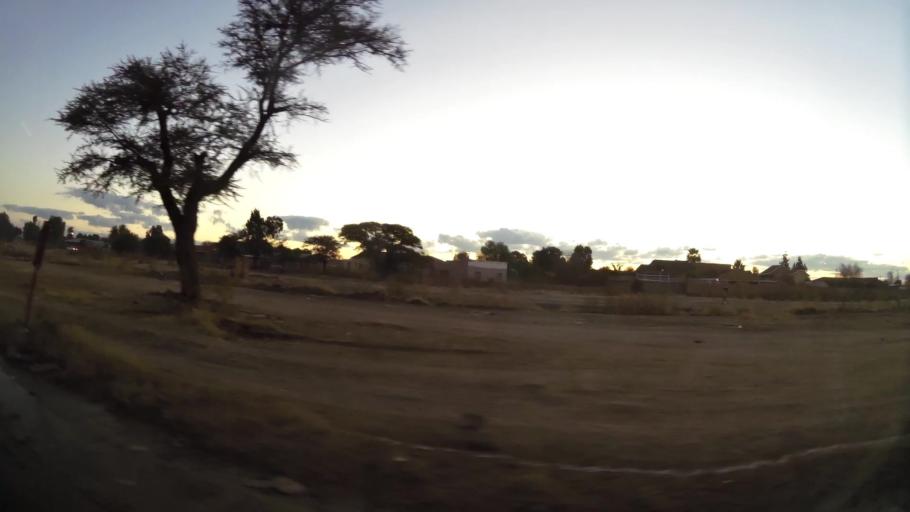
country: ZA
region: Northern Cape
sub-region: Frances Baard District Municipality
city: Kimberley
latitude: -28.7172
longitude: 24.7632
